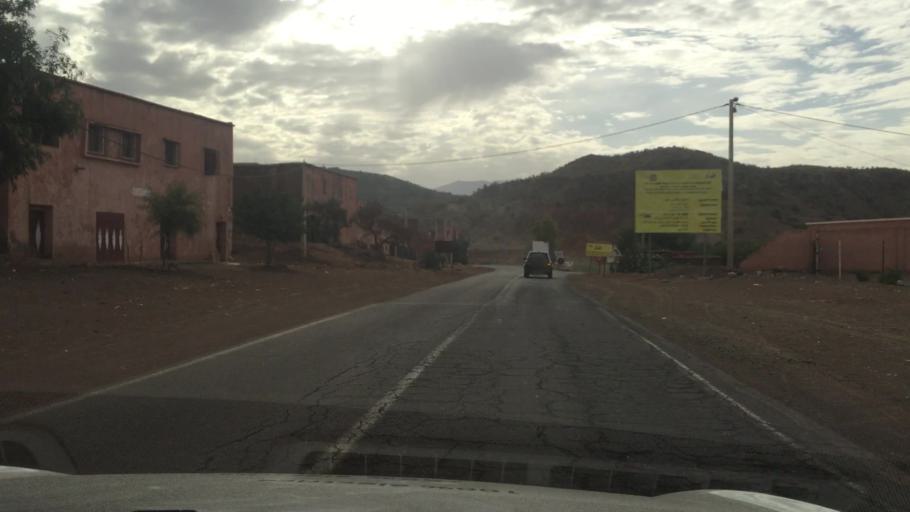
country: MA
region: Marrakech-Tensift-Al Haouz
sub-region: Al-Haouz
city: Touama
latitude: 31.5466
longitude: -7.5733
